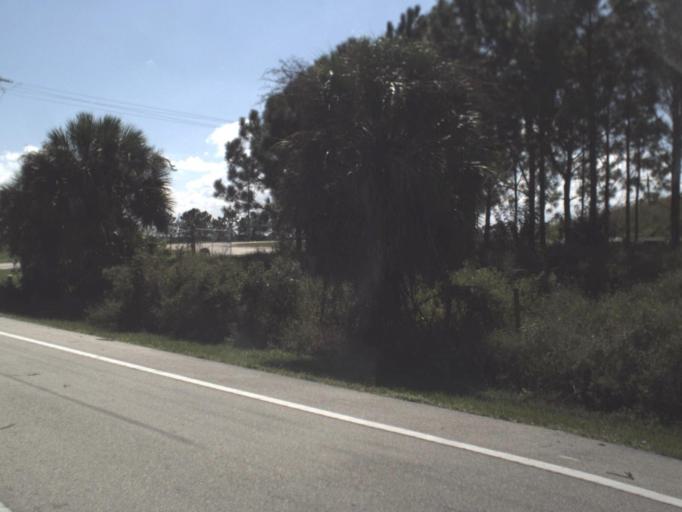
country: US
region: Florida
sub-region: Hendry County
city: Port LaBelle
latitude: 26.8133
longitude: -81.2792
